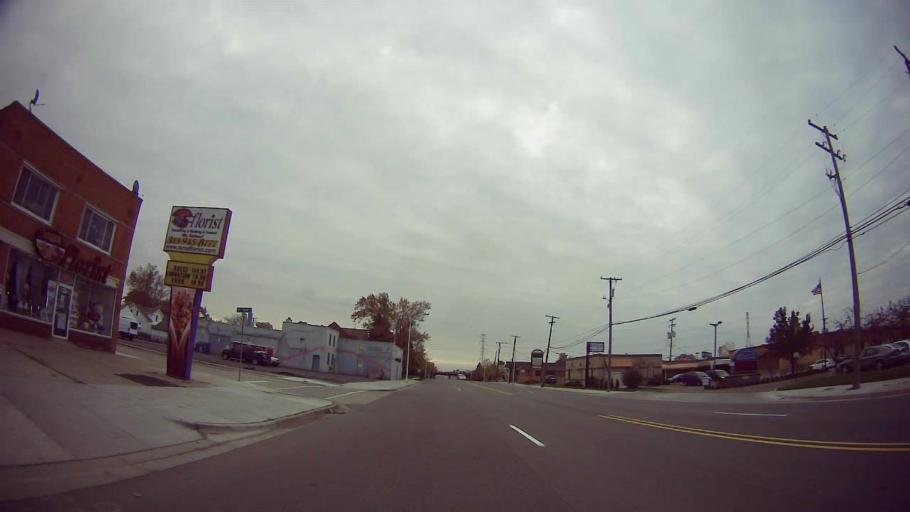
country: US
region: Michigan
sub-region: Wayne County
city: Dearborn
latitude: 42.3370
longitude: -83.1765
